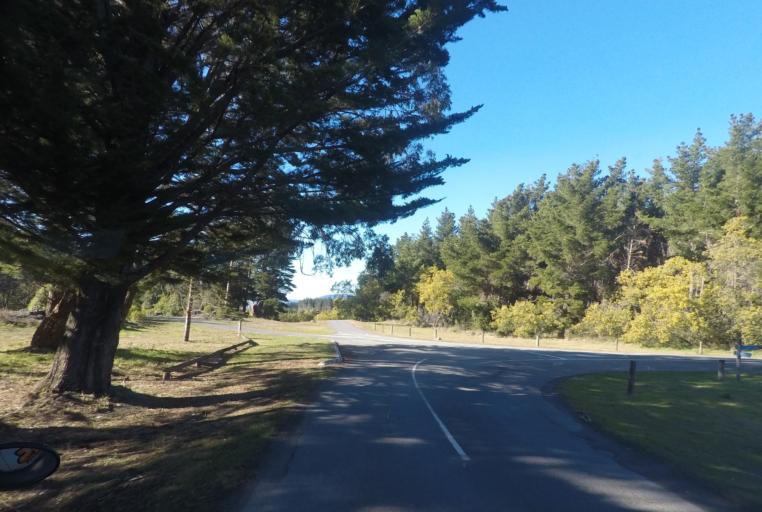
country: NZ
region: Tasman
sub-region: Tasman District
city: Mapua
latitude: -41.2675
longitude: 173.1518
